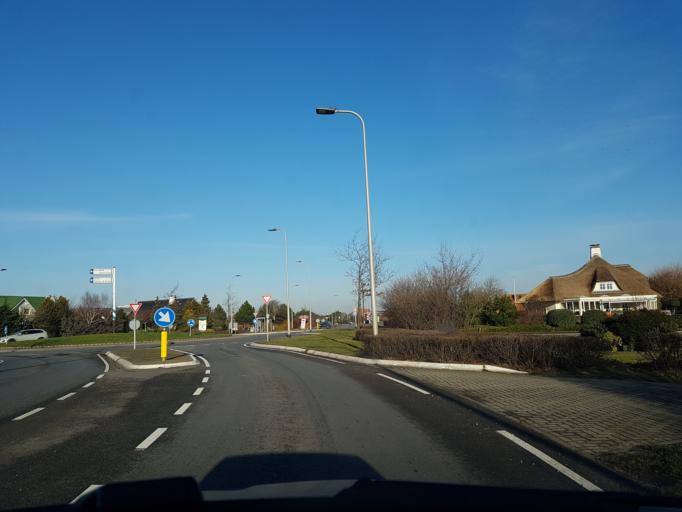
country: NL
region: South Holland
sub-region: Gemeente Noordwijk
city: Noordwijk-Binnen
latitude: 52.2212
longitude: 4.4403
